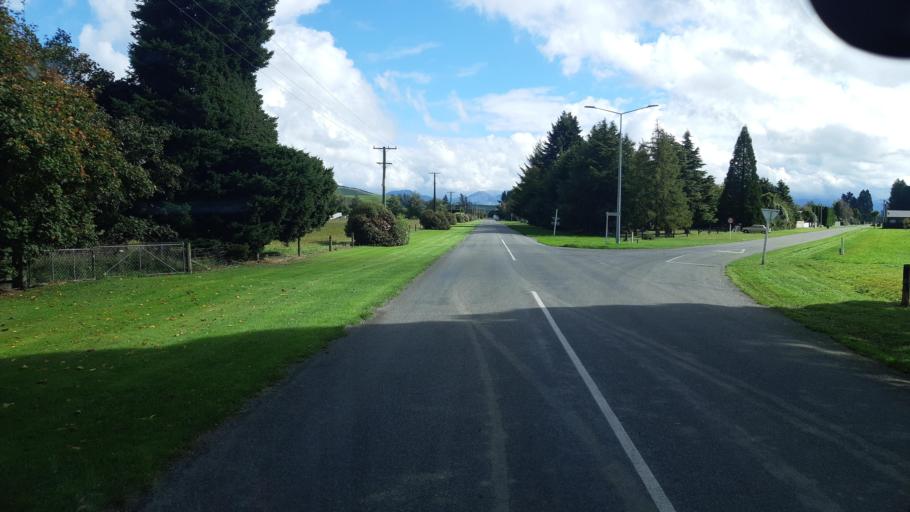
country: NZ
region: Canterbury
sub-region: Selwyn District
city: Darfield
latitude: -43.4008
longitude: 172.0406
